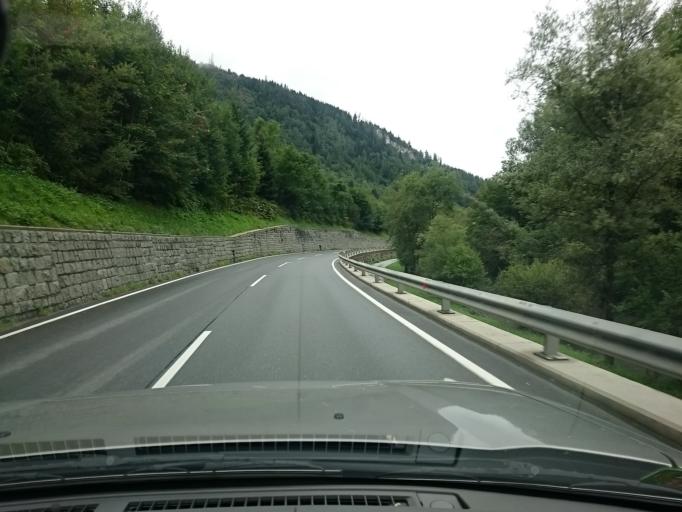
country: AT
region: Salzburg
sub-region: Politischer Bezirk Zell am See
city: Bruck an der Grossglocknerstrasse
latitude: 47.2612
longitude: 12.8253
